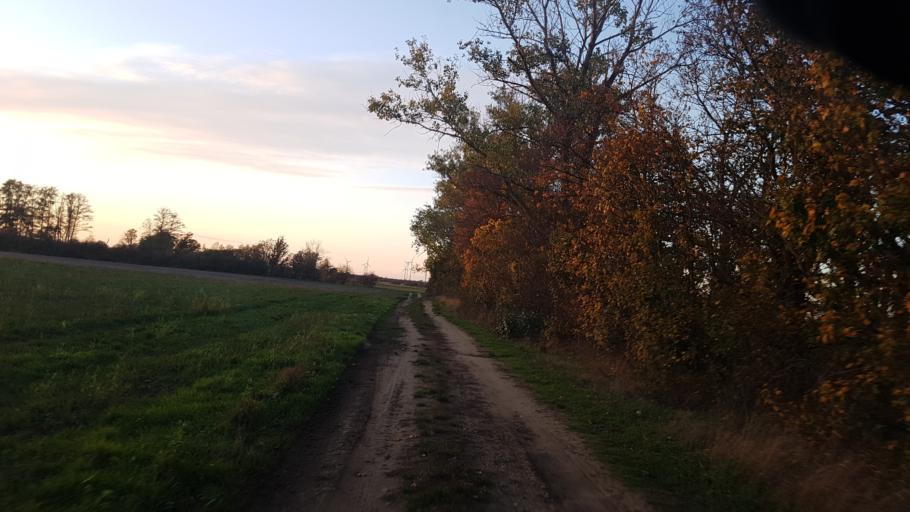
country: DE
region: Brandenburg
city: Muhlberg
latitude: 51.4971
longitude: 13.2728
